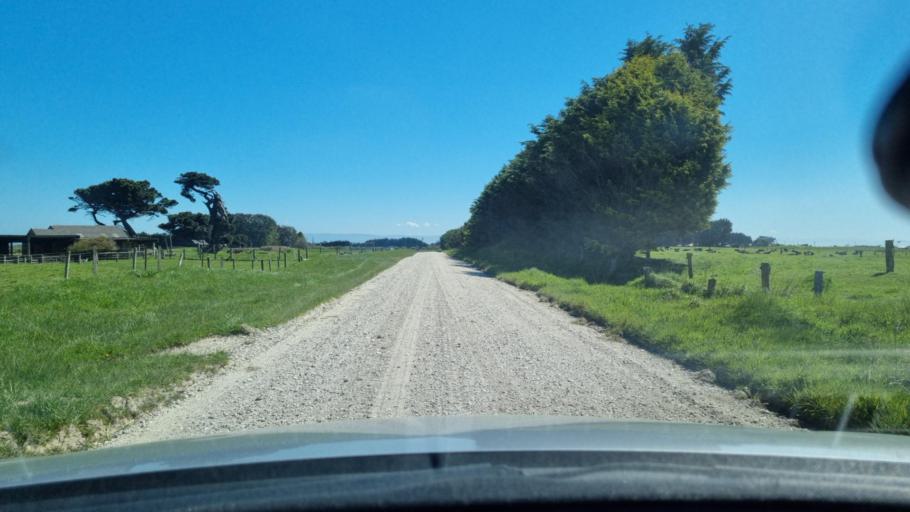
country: NZ
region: Southland
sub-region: Invercargill City
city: Invercargill
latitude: -46.4178
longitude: 168.2682
